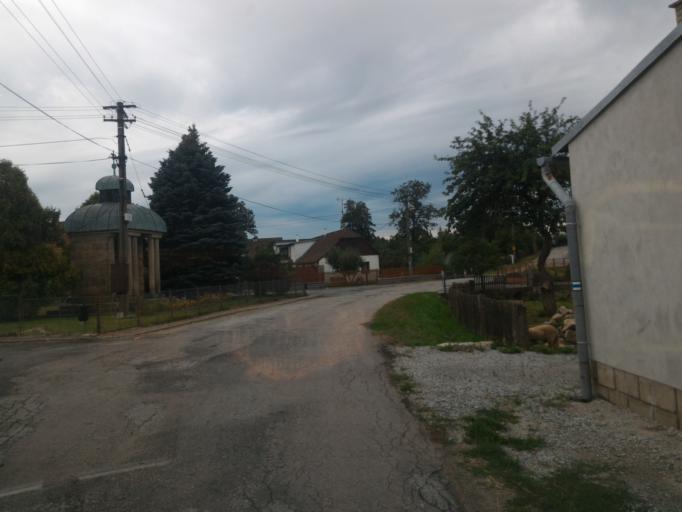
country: CZ
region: Vysocina
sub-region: Okres Jihlava
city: Telc
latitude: 49.1764
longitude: 15.3804
